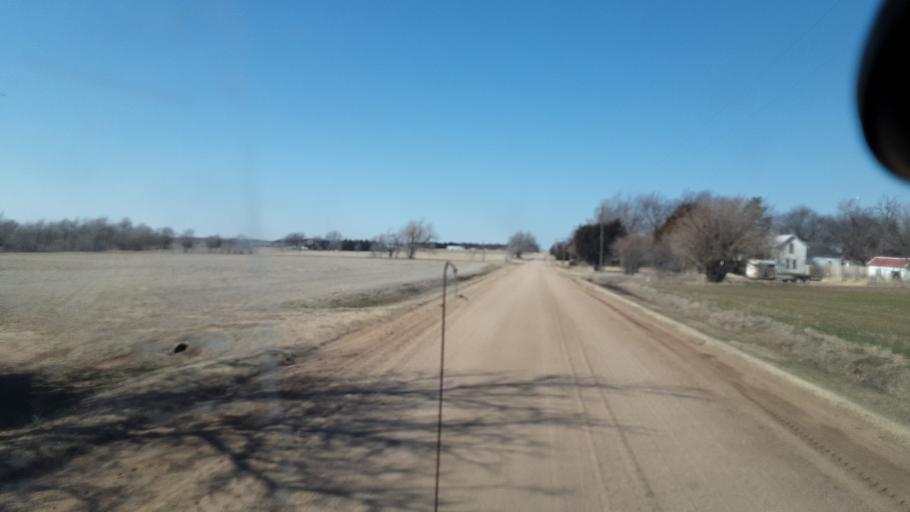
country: US
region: Kansas
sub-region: Reno County
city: South Hutchinson
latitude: 37.9846
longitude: -98.0291
